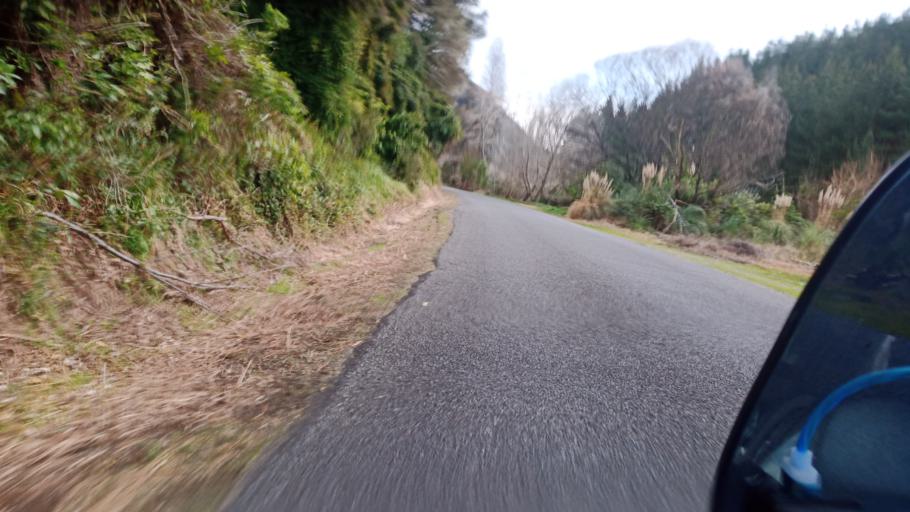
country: NZ
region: Hawke's Bay
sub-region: Wairoa District
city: Wairoa
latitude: -38.8249
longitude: 177.5101
